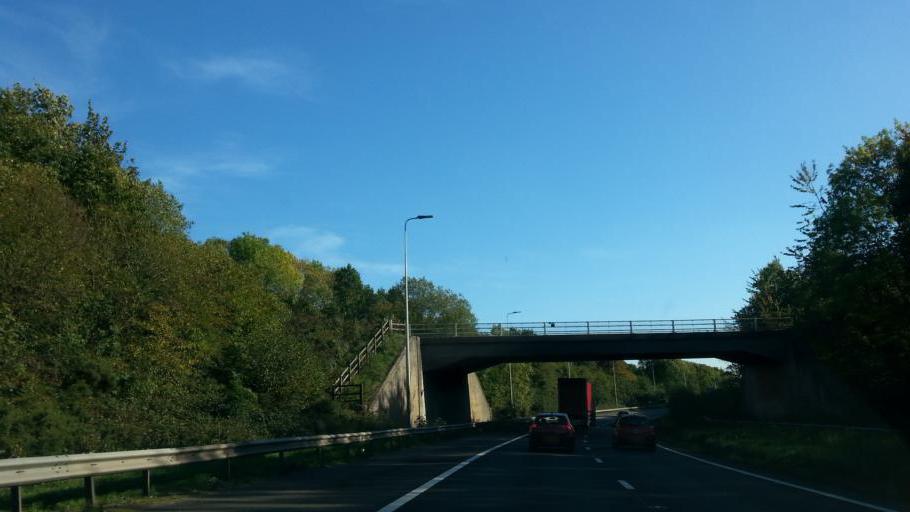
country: GB
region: England
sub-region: Staffordshire
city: Essington
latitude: 52.6357
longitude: -2.0511
